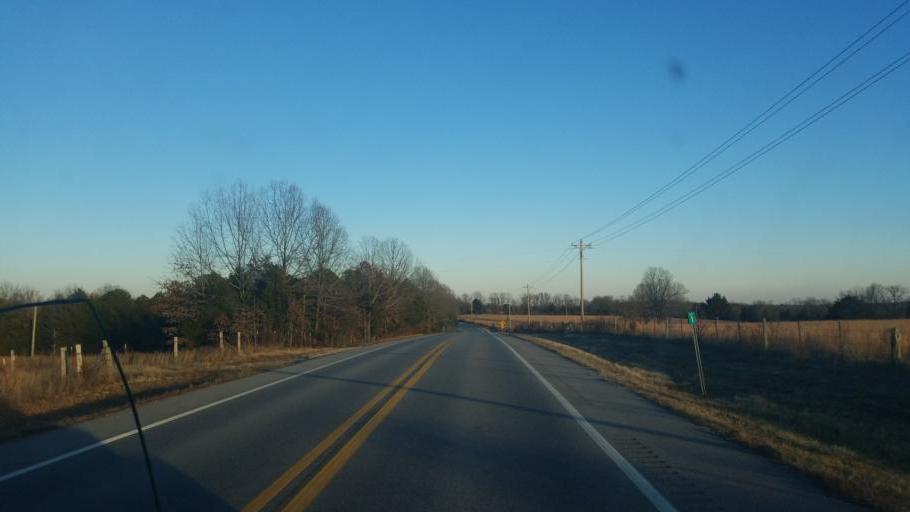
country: US
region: Arkansas
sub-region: Baxter County
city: Mountain Home
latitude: 36.3757
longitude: -92.1423
